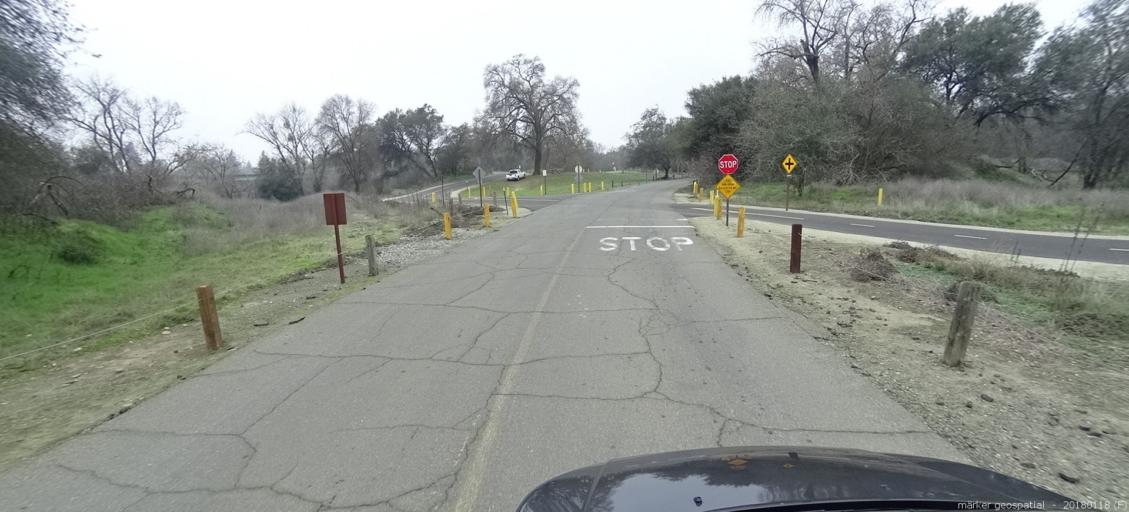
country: US
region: California
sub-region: Sacramento County
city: Rancho Cordova
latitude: 38.5924
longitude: -121.3270
